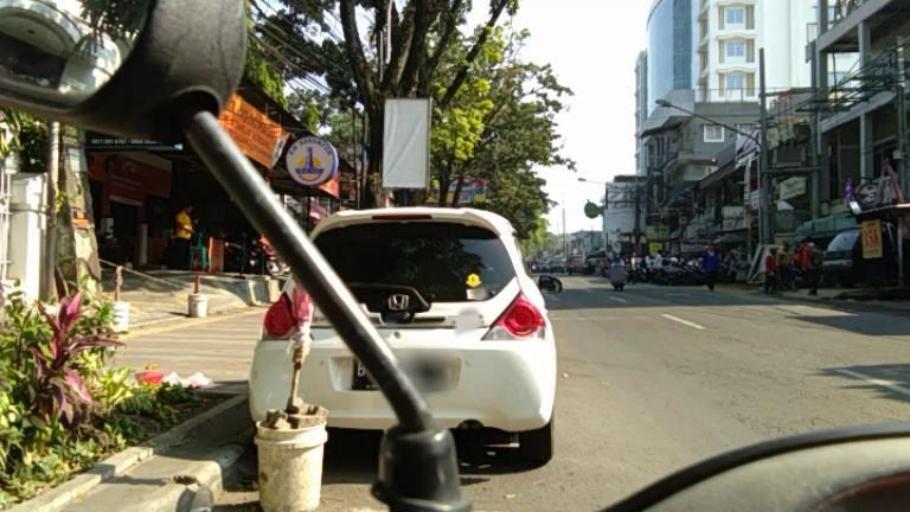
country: ID
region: West Java
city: Bandung
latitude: -6.8881
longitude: 107.6155
